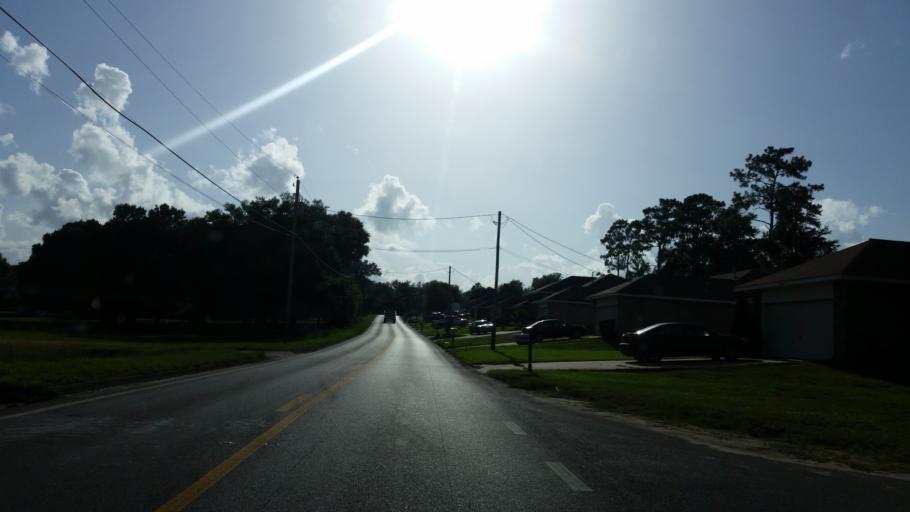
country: US
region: Florida
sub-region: Santa Rosa County
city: Bagdad
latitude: 30.5800
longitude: -87.0440
